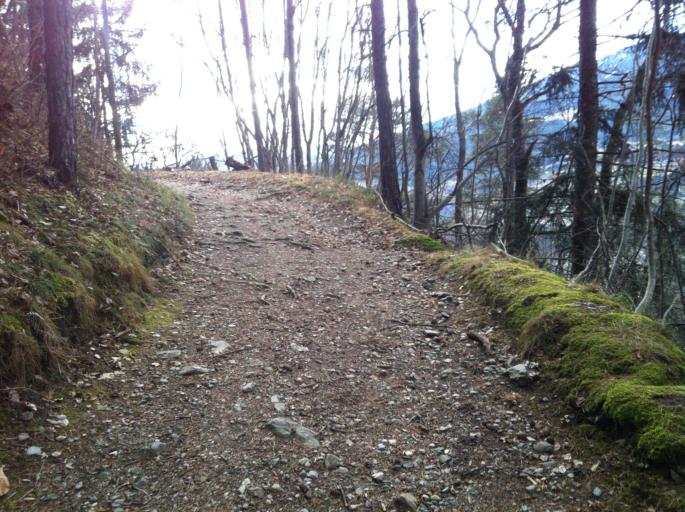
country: IT
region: Trentino-Alto Adige
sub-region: Bolzano
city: Bressanone
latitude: 46.6933
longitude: 11.6631
